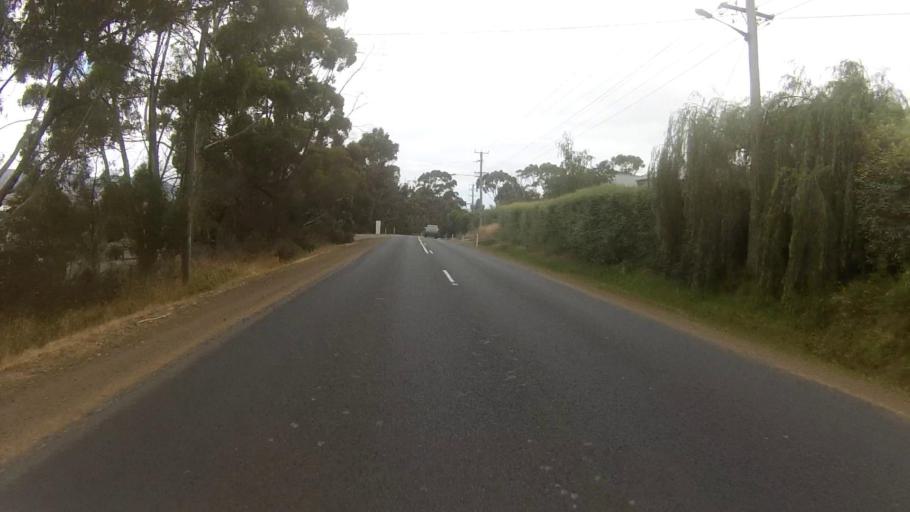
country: AU
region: Tasmania
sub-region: Kingborough
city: Margate
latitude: -43.0165
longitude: 147.2519
